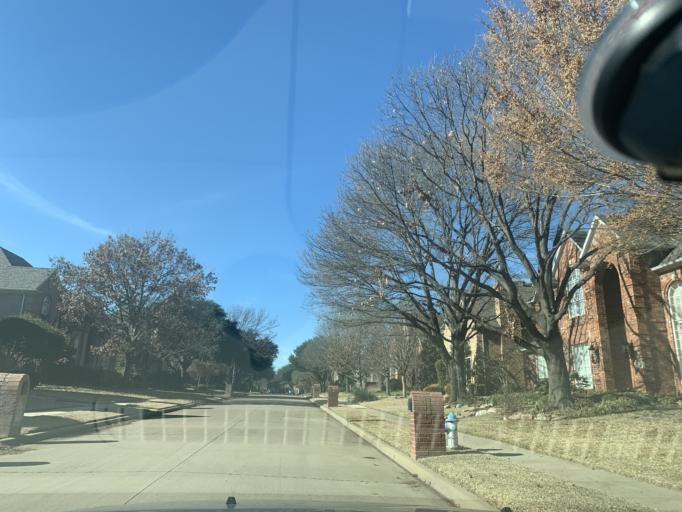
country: US
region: Texas
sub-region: Denton County
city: The Colony
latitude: 33.0512
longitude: -96.8134
